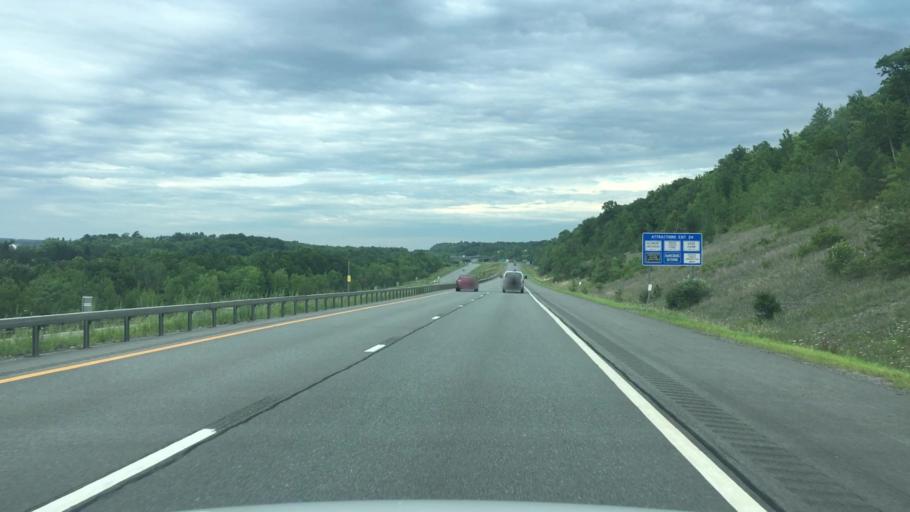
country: US
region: New York
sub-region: Albany County
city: Altamont
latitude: 42.7555
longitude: -74.1361
